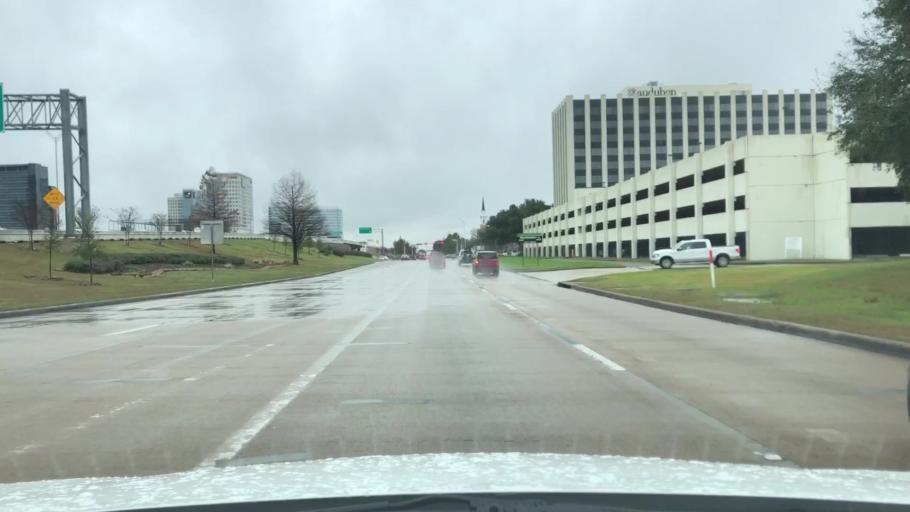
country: US
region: Texas
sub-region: Harris County
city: Bunker Hill Village
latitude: 29.7342
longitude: -95.5570
